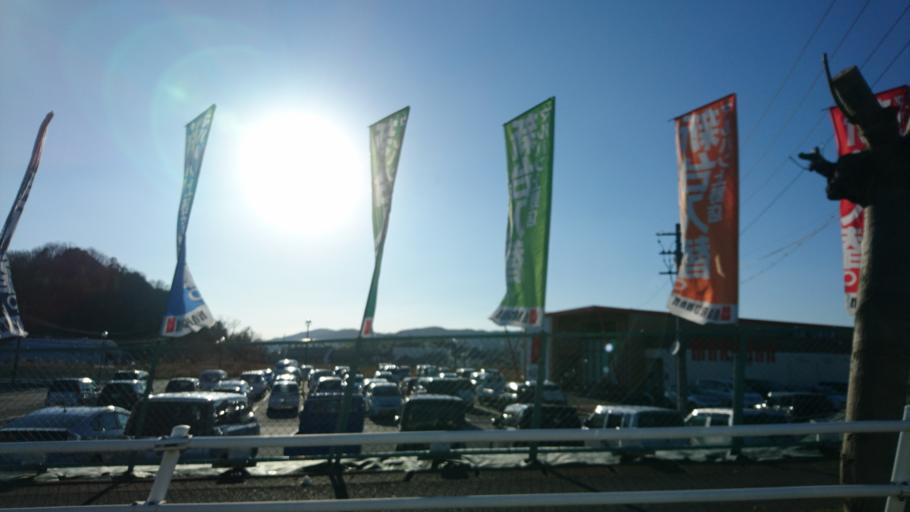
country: JP
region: Mie
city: Ueno-ebisumachi
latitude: 34.7557
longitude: 136.1326
